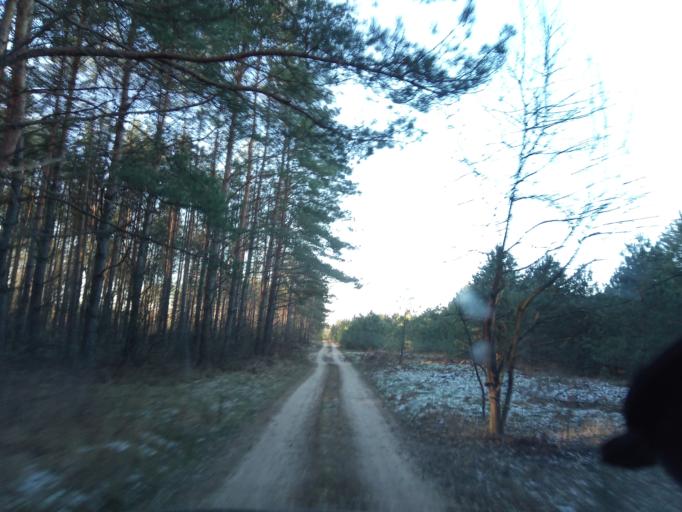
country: LT
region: Alytaus apskritis
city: Druskininkai
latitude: 53.9697
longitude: 23.9666
